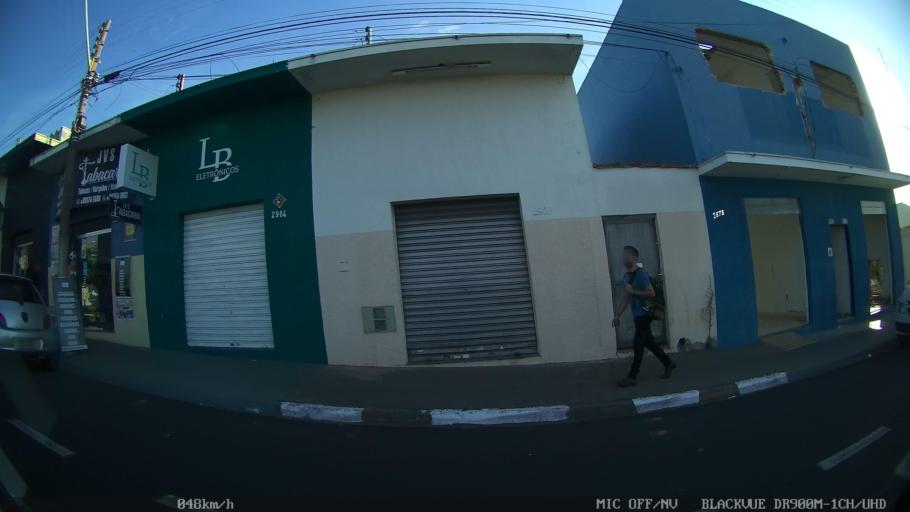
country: BR
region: Sao Paulo
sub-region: Franca
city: Franca
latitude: -20.5410
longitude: -47.3878
